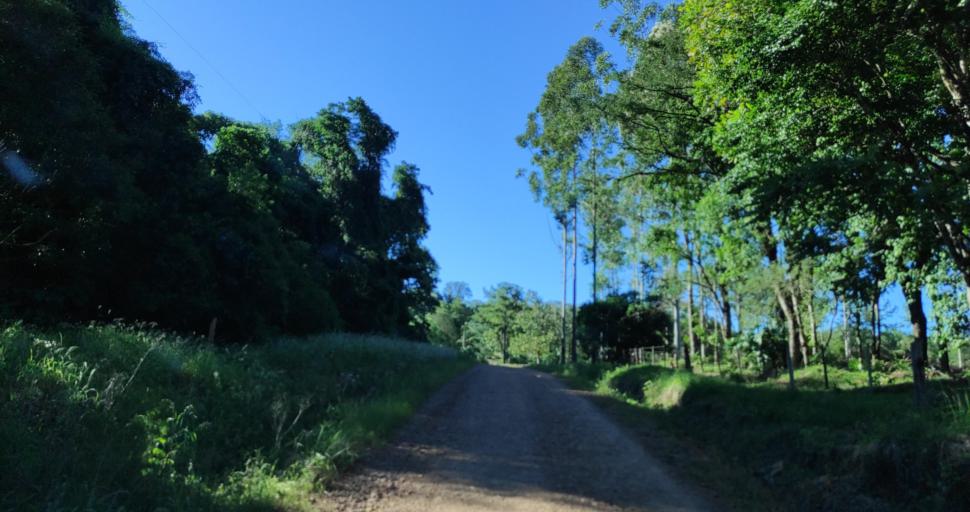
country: AR
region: Misiones
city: Capiovi
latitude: -26.9085
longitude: -54.9991
